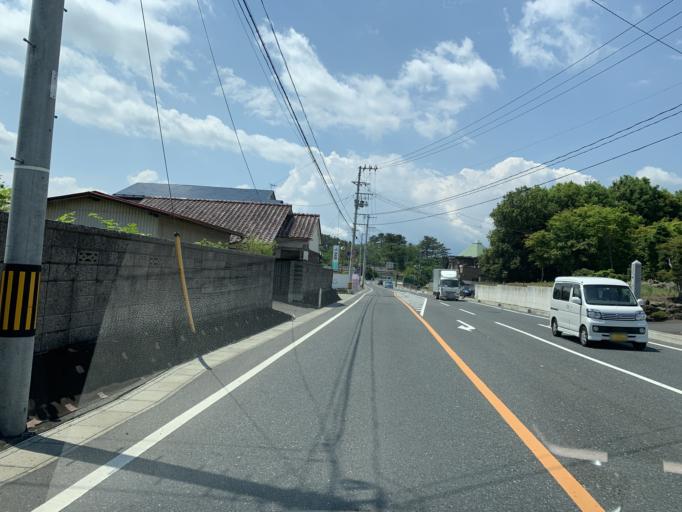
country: JP
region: Miyagi
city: Kogota
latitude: 38.5406
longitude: 141.0580
